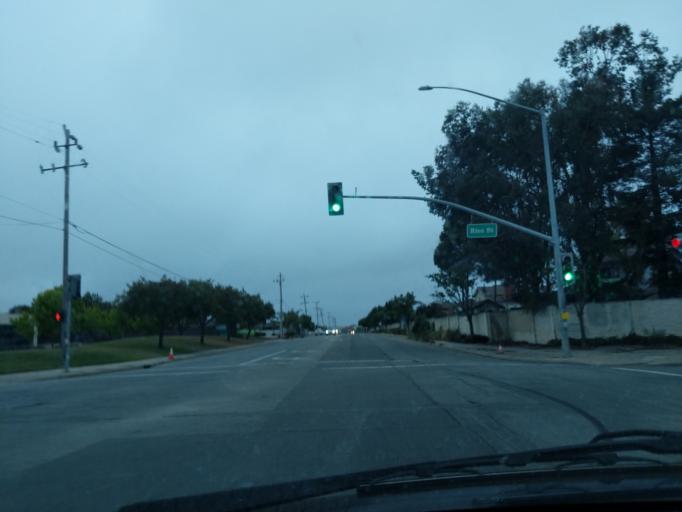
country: US
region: California
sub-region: Monterey County
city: Salinas
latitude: 36.6839
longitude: -121.6615
